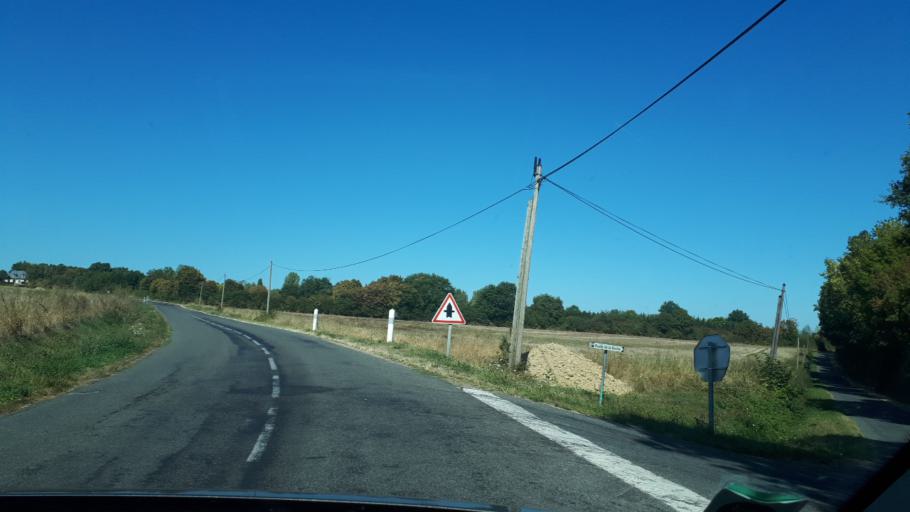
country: FR
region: Centre
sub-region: Departement du Loiret
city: Autry-le-Chatel
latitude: 47.6054
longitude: 2.5872
